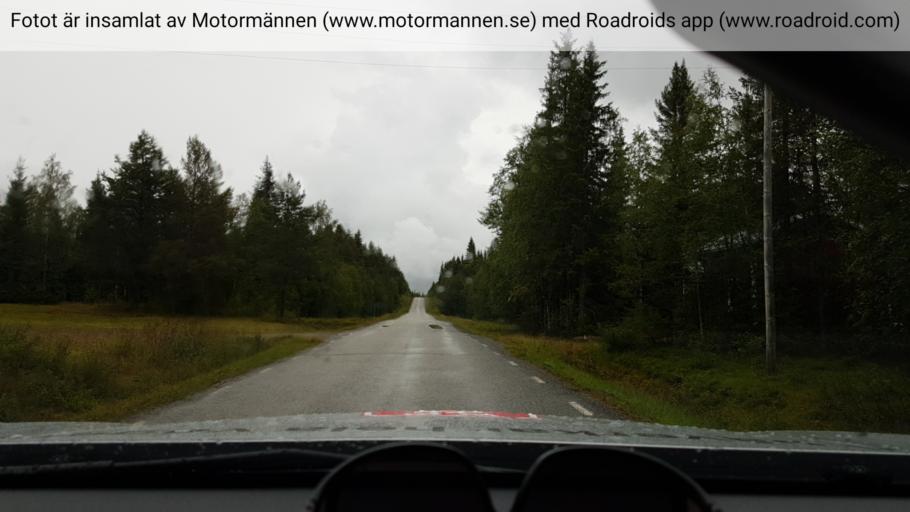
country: SE
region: Vaesterbotten
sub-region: Asele Kommun
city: Insjon
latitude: 64.8064
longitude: 17.5359
